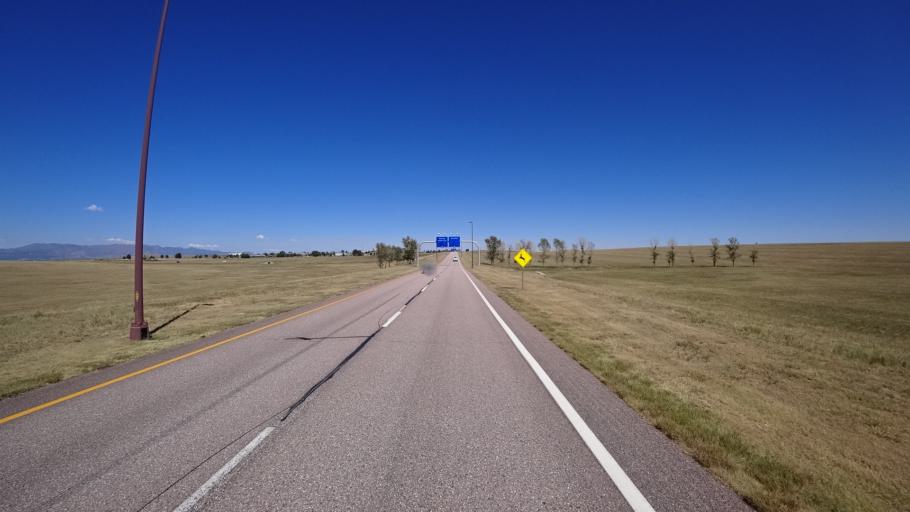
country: US
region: Colorado
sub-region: El Paso County
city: Security-Widefield
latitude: 38.7850
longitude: -104.6974
